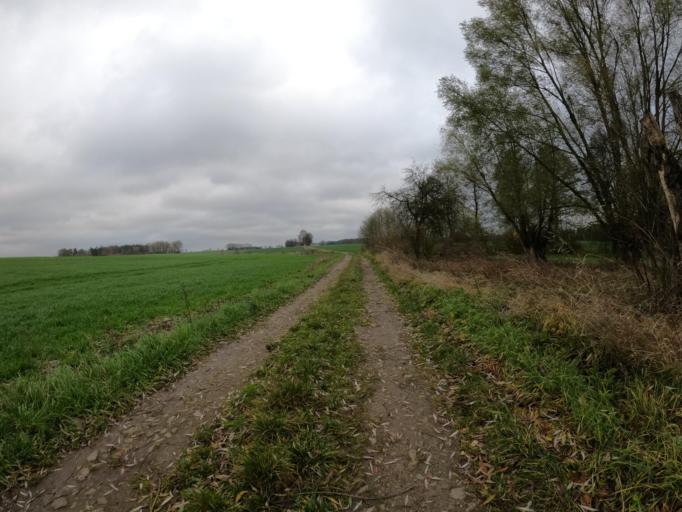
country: PL
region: West Pomeranian Voivodeship
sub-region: Powiat walecki
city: Tuczno
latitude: 53.2752
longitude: 16.1642
